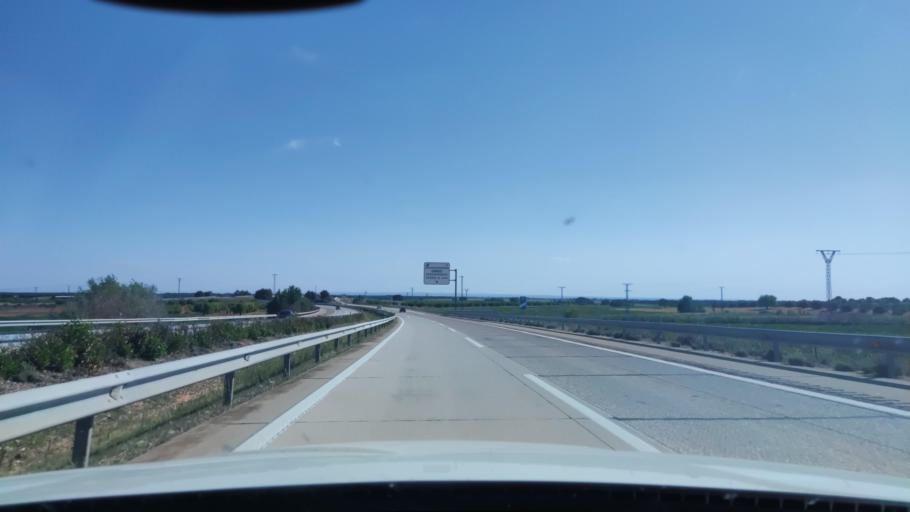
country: ES
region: Castille-La Mancha
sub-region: Provincia de Cuenca
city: Pozoamargo
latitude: 39.3659
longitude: -2.2026
